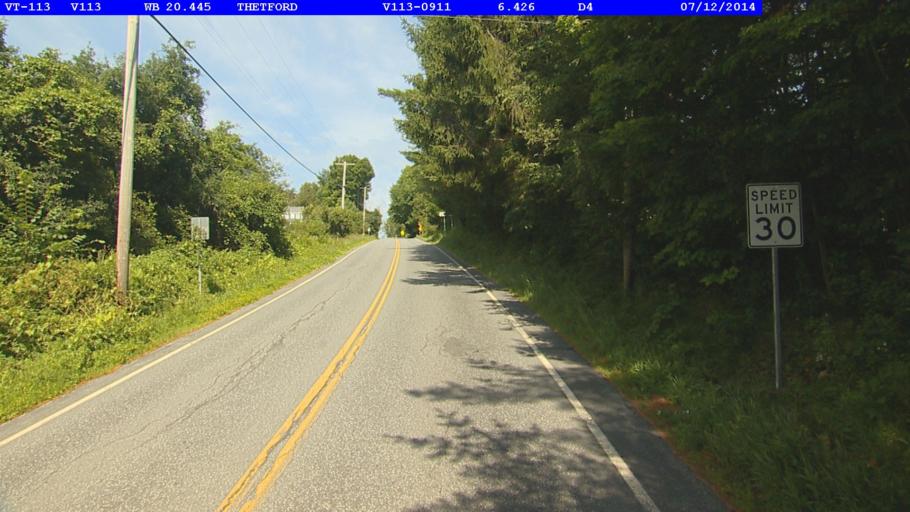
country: US
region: New Hampshire
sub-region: Grafton County
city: Lyme
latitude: 43.8183
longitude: -72.2254
